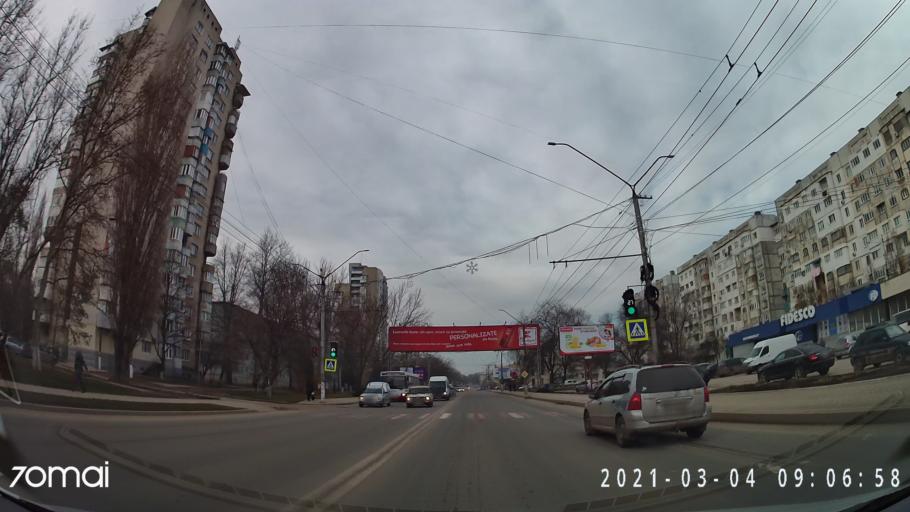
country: MD
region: Balti
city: Balti
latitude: 47.7674
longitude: 27.9389
